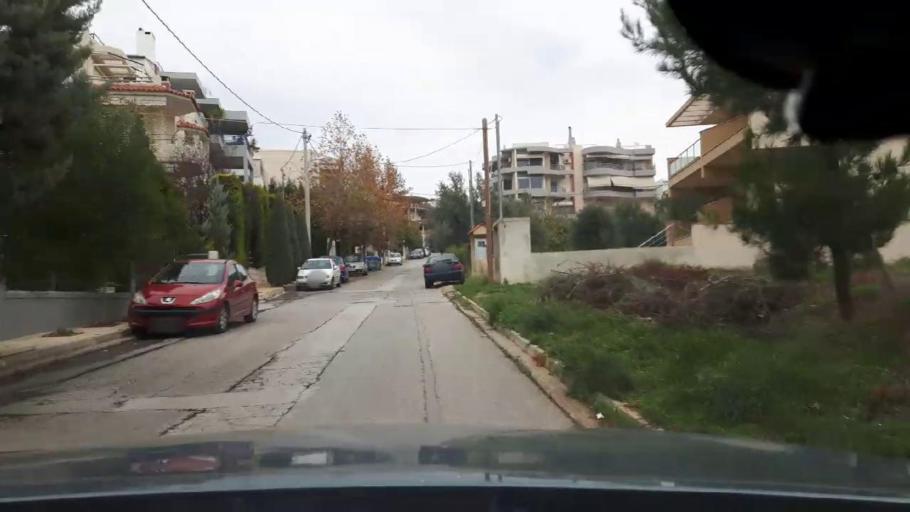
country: GR
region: Attica
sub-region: Nomarchia Athinas
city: Melissia
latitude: 38.0502
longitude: 23.8299
